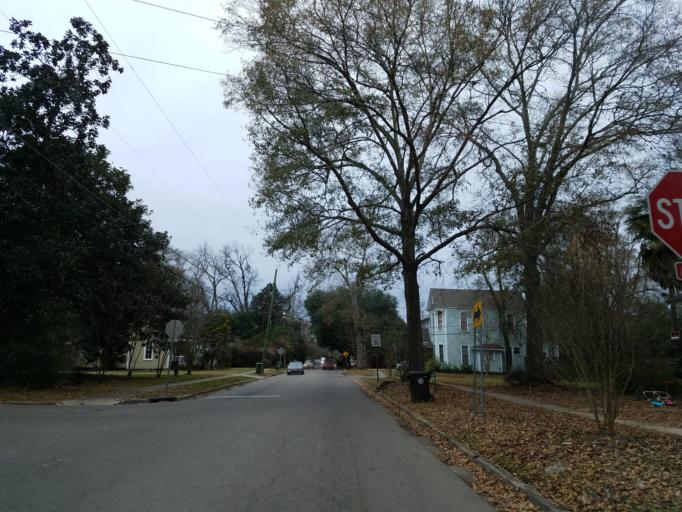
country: US
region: Mississippi
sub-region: Forrest County
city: Hattiesburg
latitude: 31.3218
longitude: -89.2843
